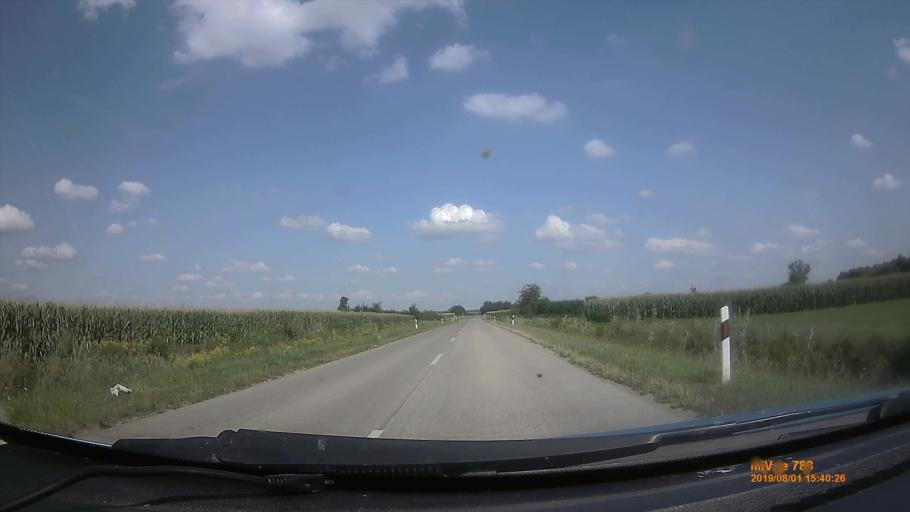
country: HU
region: Baranya
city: Szentlorinc
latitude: 45.9876
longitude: 17.9525
